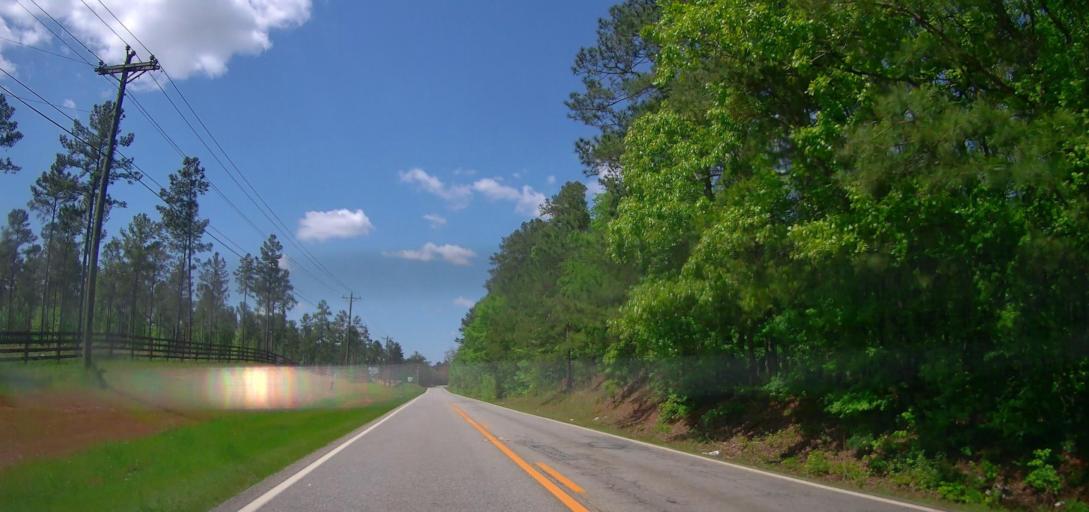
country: US
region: Georgia
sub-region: Putnam County
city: Eatonton
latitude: 33.2762
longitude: -83.3023
